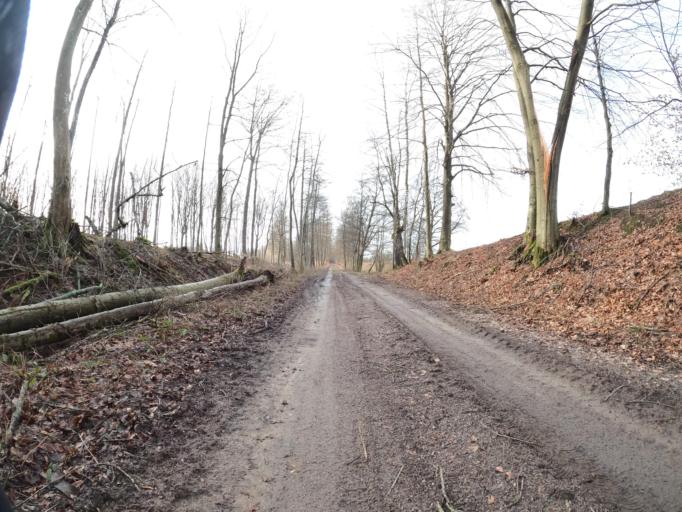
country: PL
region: West Pomeranian Voivodeship
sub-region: Powiat koszalinski
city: Polanow
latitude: 54.1746
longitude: 16.7437
